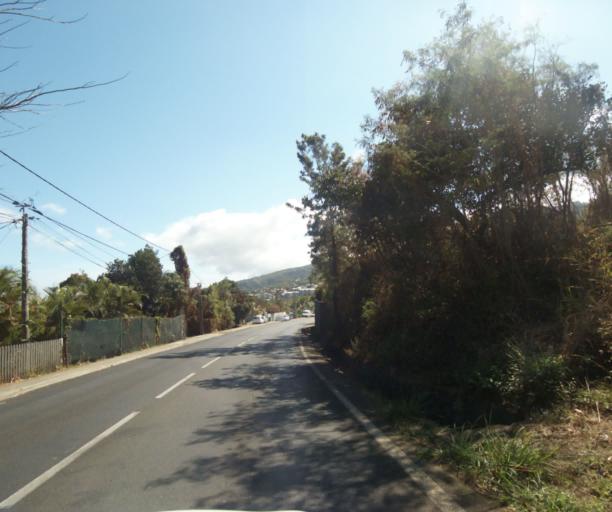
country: RE
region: Reunion
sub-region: Reunion
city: La Possession
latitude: -20.9870
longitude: 55.3321
